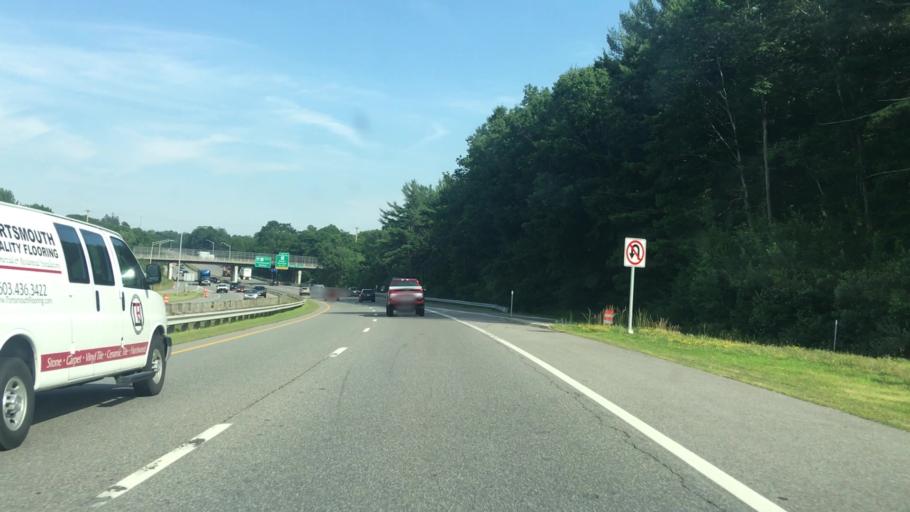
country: US
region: New Hampshire
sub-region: Strafford County
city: Dover
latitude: 43.1840
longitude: -70.8856
